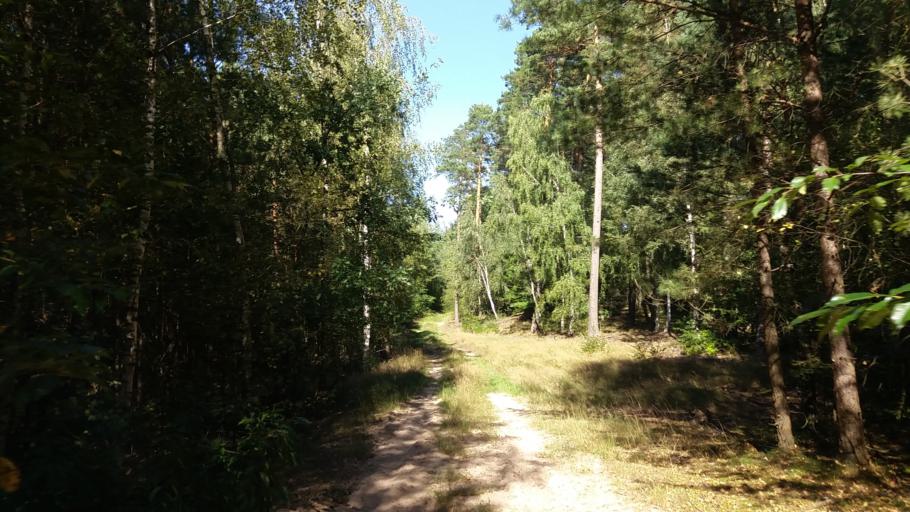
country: PL
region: West Pomeranian Voivodeship
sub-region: Powiat choszczenski
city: Krzecin
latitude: 53.0872
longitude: 15.4602
